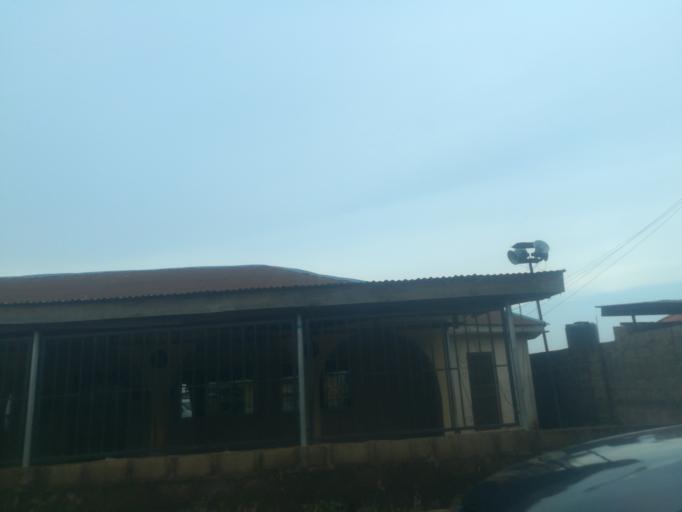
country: NG
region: Oyo
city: Ibadan
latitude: 7.3529
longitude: 3.8248
